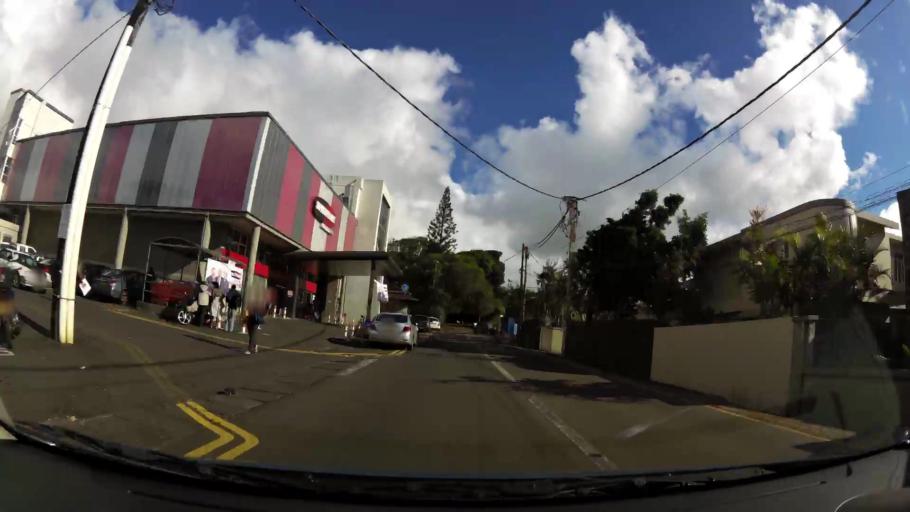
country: MU
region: Plaines Wilhems
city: Curepipe
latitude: -20.3229
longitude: 57.5184
